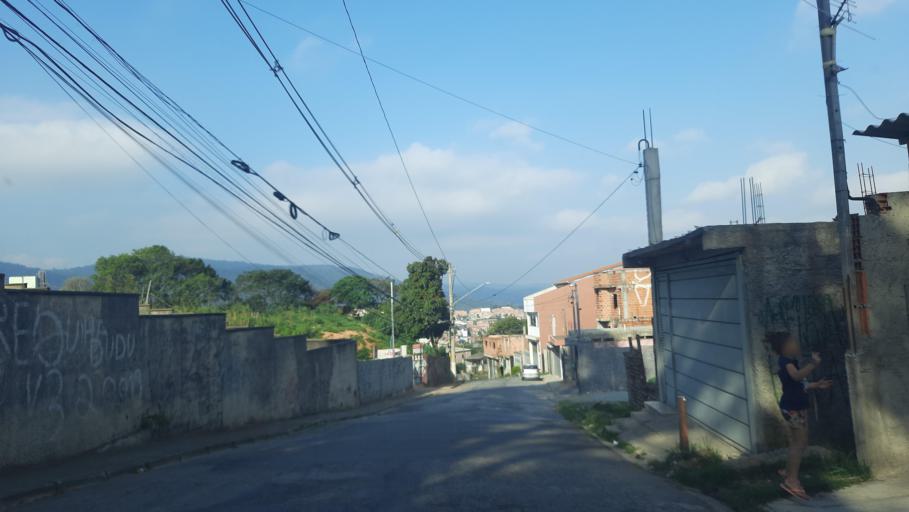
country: BR
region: Sao Paulo
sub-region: Caieiras
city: Caieiras
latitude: -23.4522
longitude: -46.7173
